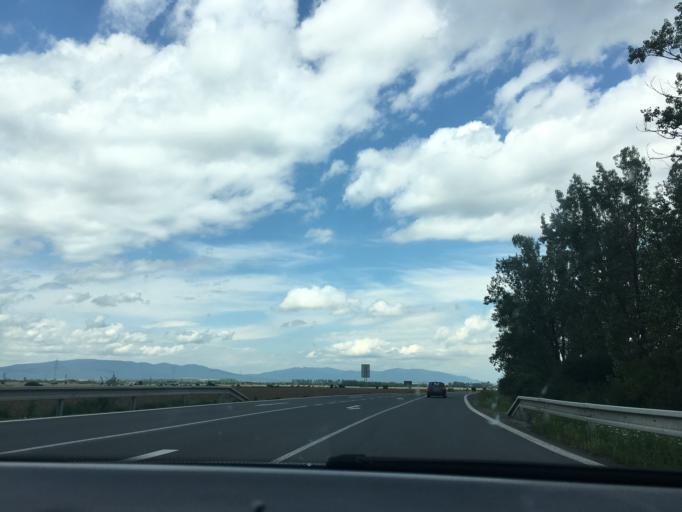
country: SK
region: Kosicky
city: Trebisov
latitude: 48.6032
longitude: 21.7108
